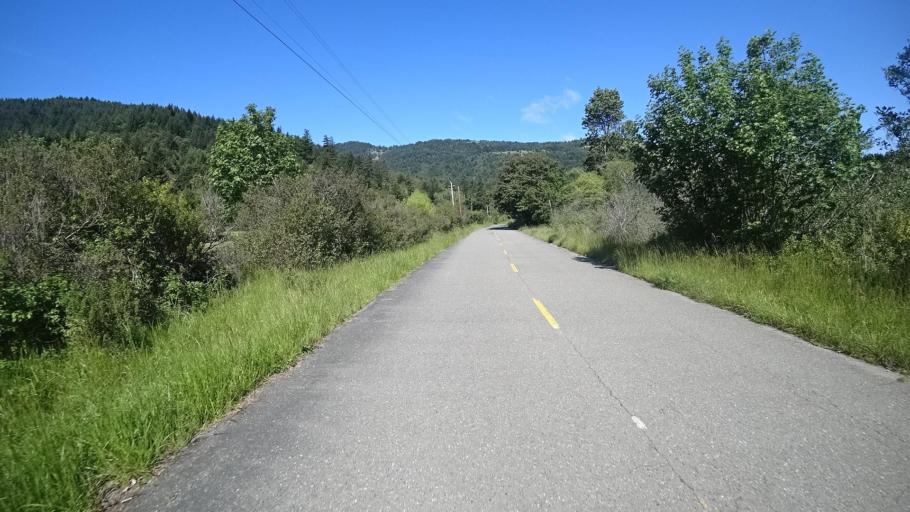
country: US
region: California
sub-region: Humboldt County
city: Rio Dell
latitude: 40.2796
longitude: -124.2466
